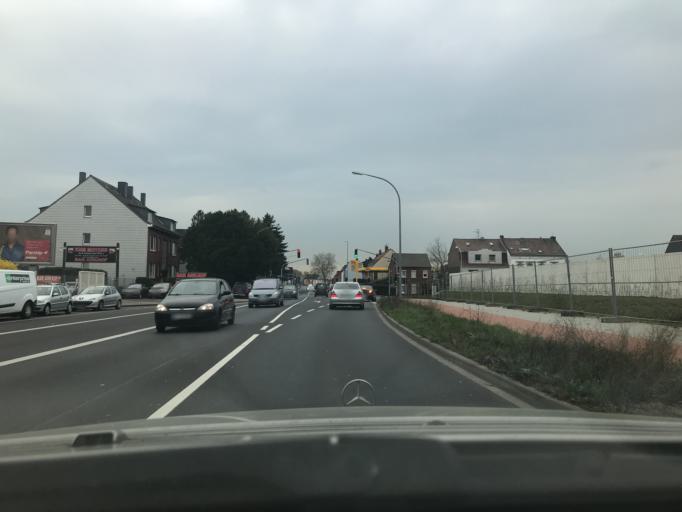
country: DE
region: North Rhine-Westphalia
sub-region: Regierungsbezirk Dusseldorf
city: Korschenbroich
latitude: 51.2214
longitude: 6.4801
